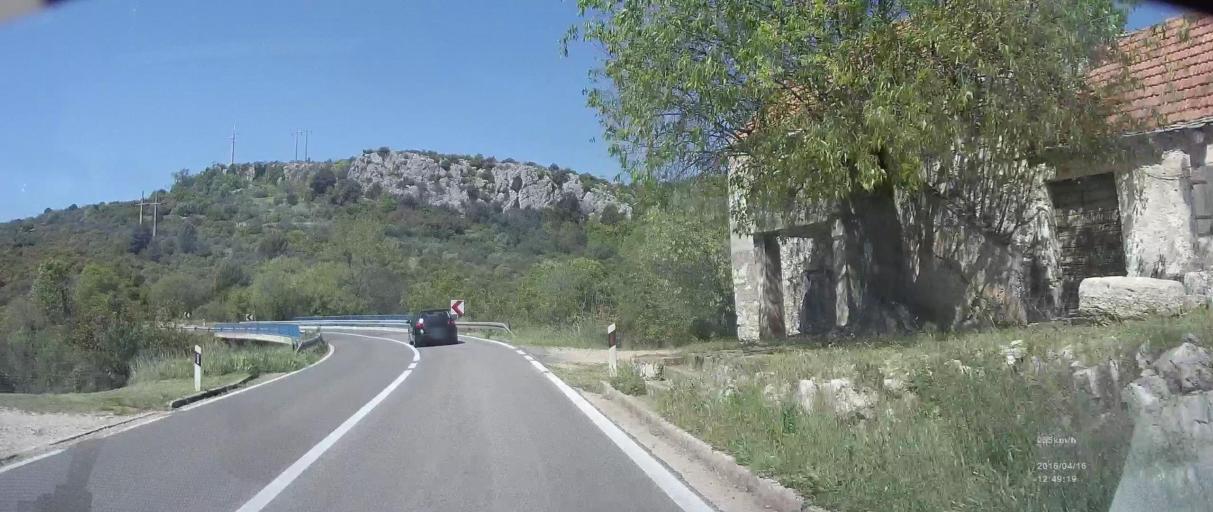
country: HR
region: Sibensko-Kniniska
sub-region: Grad Sibenik
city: Brodarica
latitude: 43.6741
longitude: 16.0276
